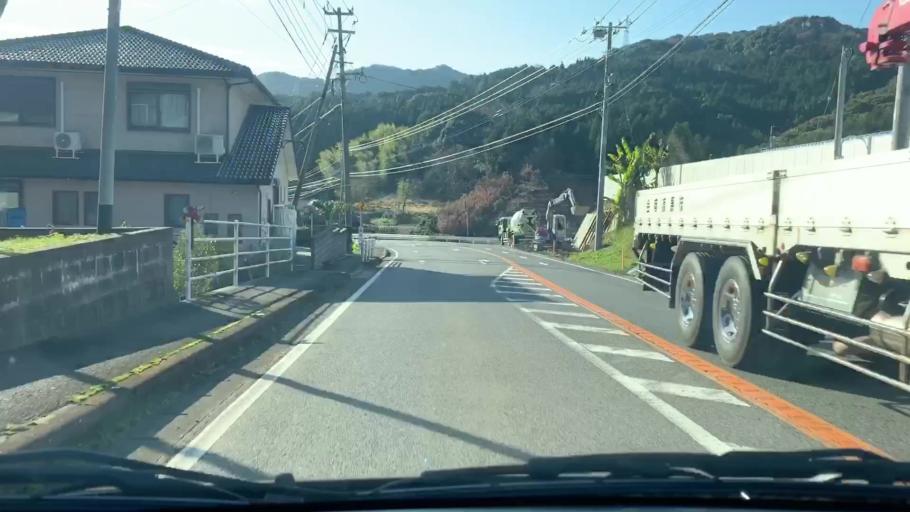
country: JP
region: Saga Prefecture
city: Takeocho-takeo
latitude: 33.2346
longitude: 130.0127
